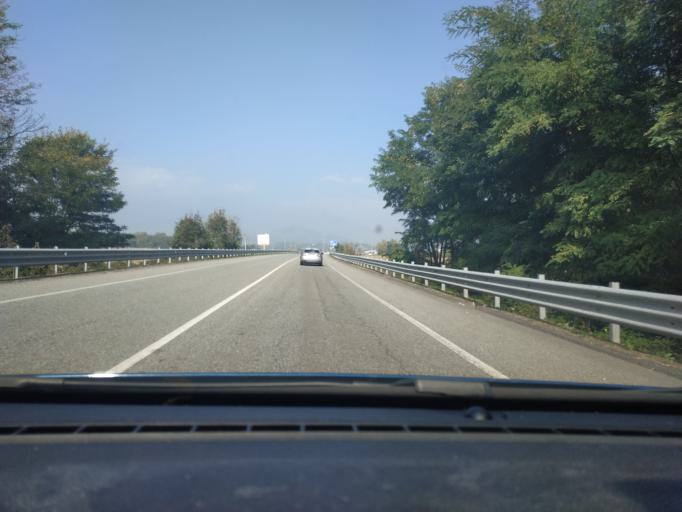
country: IT
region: Piedmont
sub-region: Provincia di Biella
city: Ponderano
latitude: 45.5365
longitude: 8.0396
